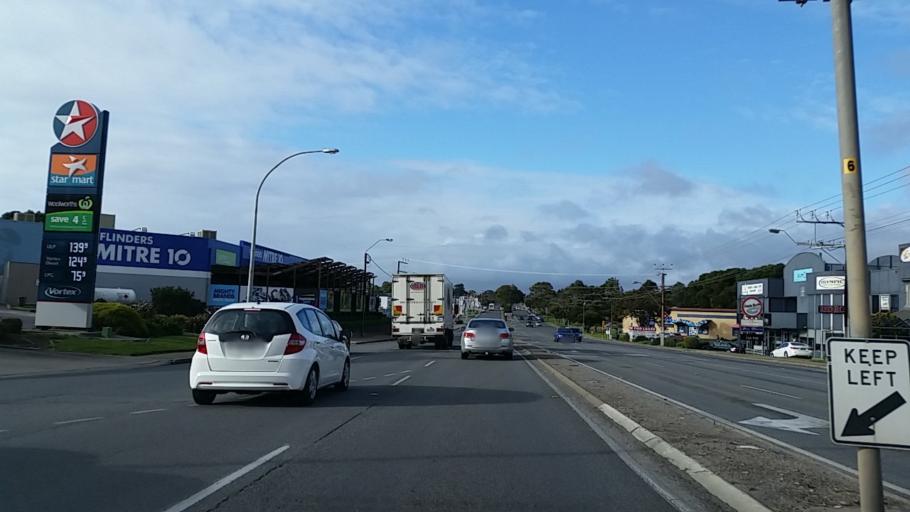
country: AU
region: South Australia
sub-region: Onkaparinga
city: Reynella
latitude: -35.1049
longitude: 138.5274
